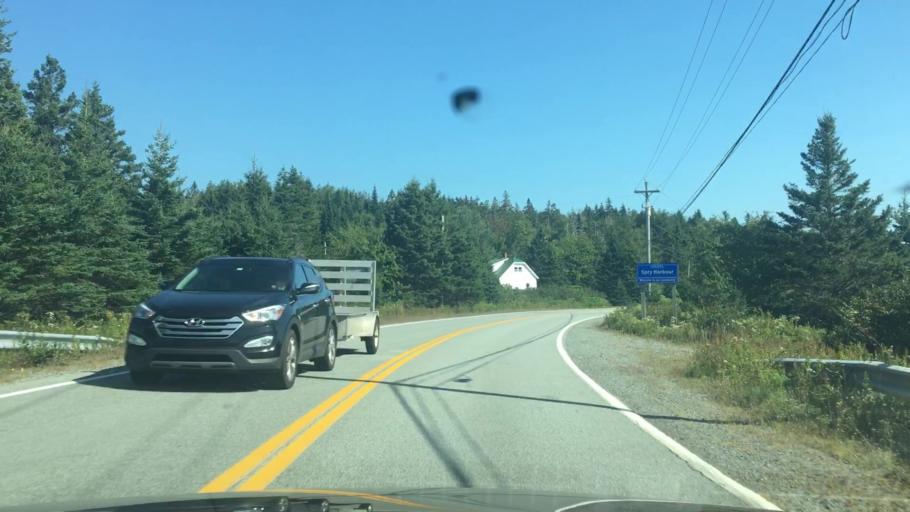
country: CA
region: Nova Scotia
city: New Glasgow
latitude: 44.8221
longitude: -62.6343
